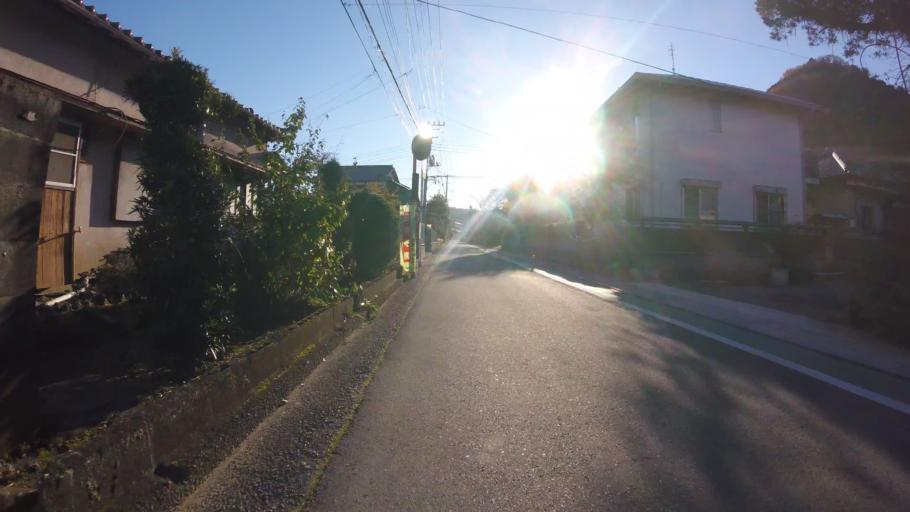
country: JP
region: Shizuoka
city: Mishima
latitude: 34.9880
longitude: 138.9460
